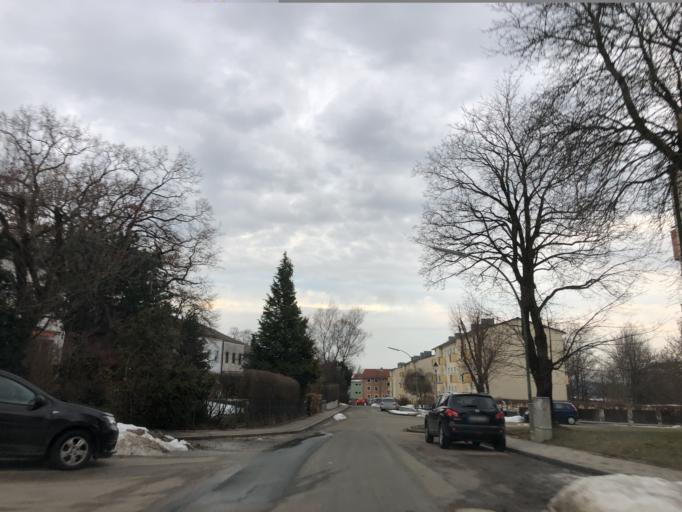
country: DE
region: Bavaria
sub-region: Upper Bavaria
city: Ebersberg
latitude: 48.0717
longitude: 11.9598
